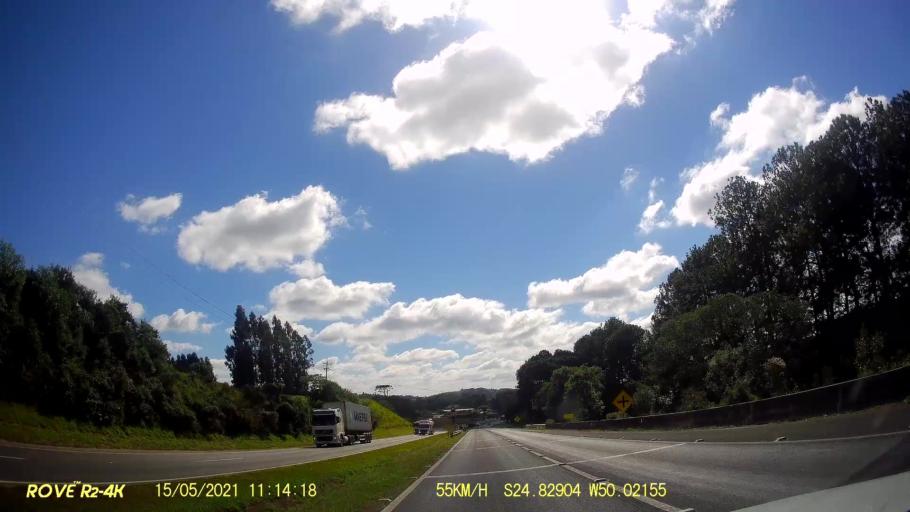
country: BR
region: Parana
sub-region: Castro
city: Castro
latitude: -24.8292
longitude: -50.0215
